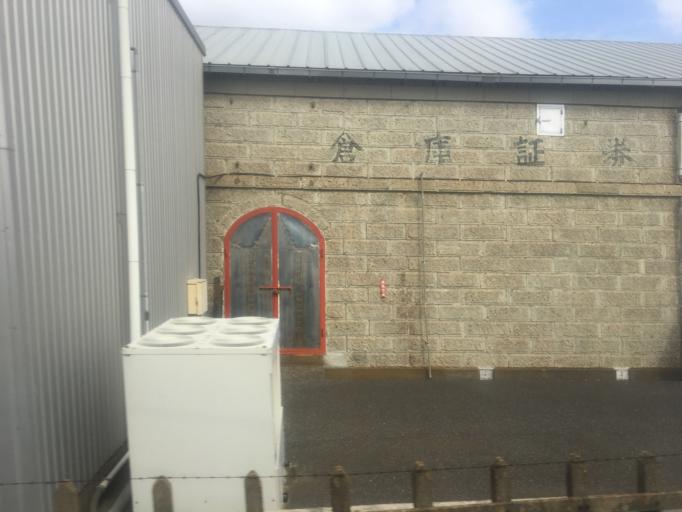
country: JP
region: Chiba
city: Yachimata
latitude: 35.6644
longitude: 140.3151
